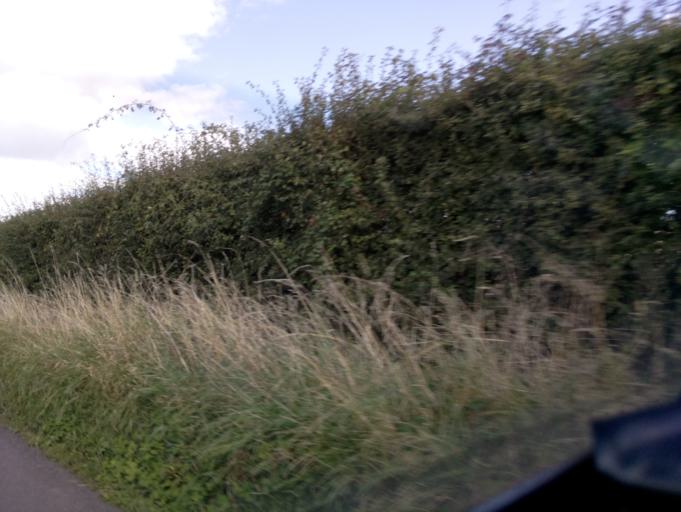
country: GB
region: England
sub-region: Wiltshire
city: Bratton
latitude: 51.2865
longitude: -2.1283
